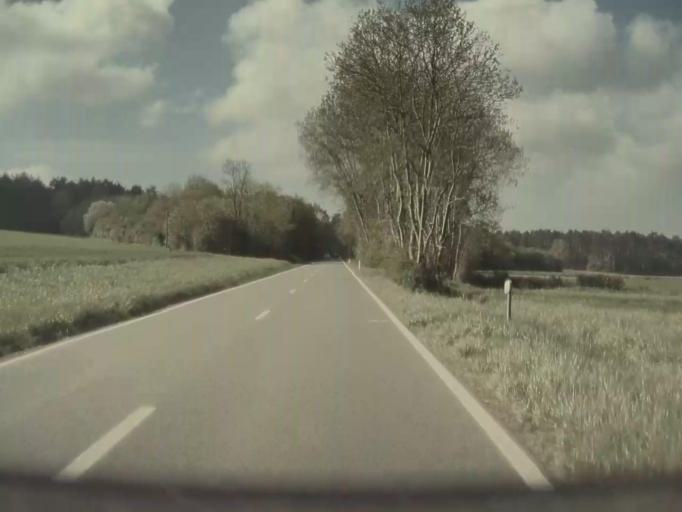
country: BE
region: Wallonia
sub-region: Province du Luxembourg
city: Tellin
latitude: 50.1041
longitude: 5.2329
